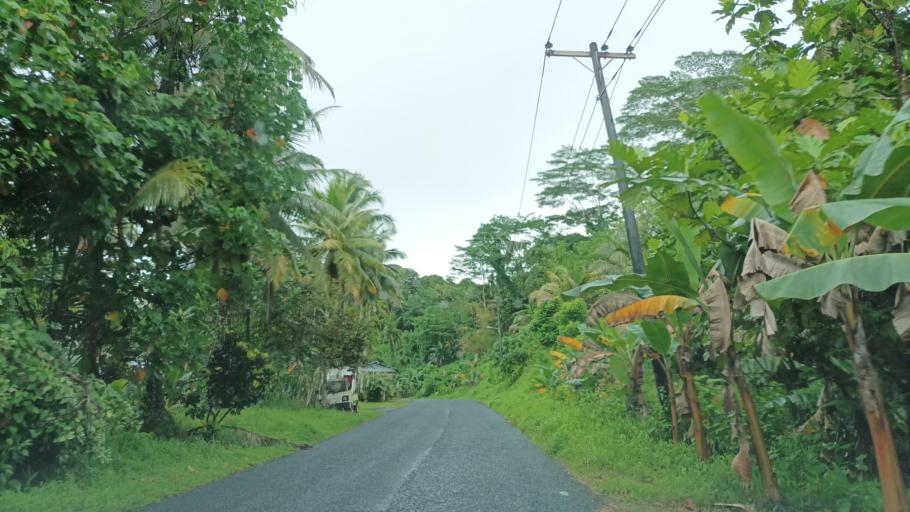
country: FM
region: Pohnpei
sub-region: Sokehs Municipality
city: Palikir - National Government Center
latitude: 6.8850
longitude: 158.1573
